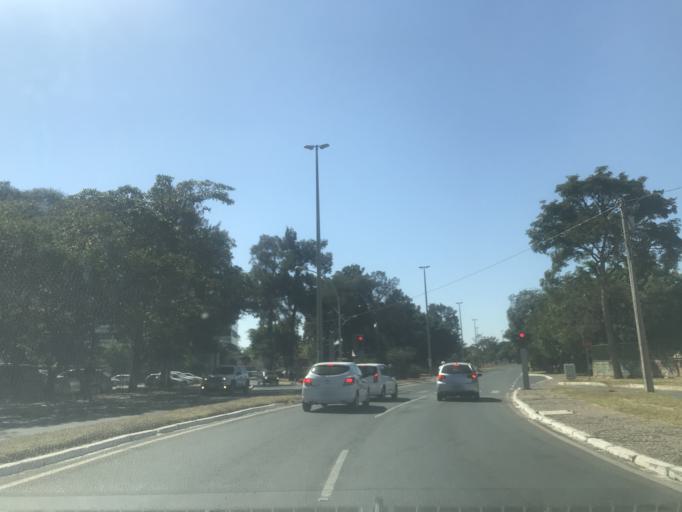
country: BR
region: Federal District
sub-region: Brasilia
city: Brasilia
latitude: -15.8187
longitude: -47.9859
